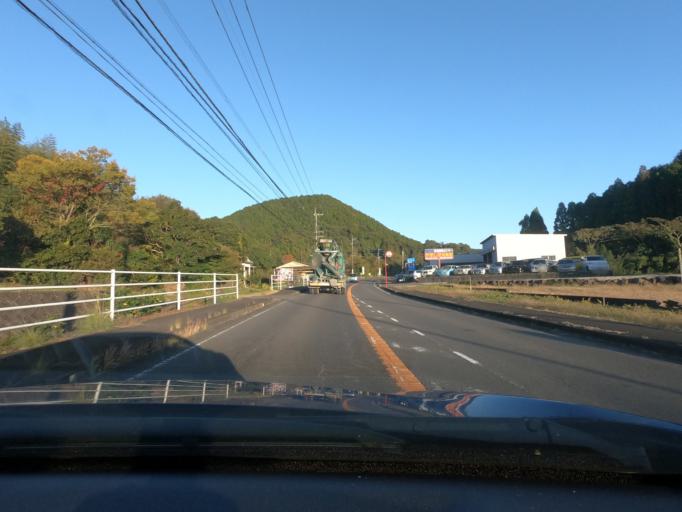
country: JP
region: Kagoshima
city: Satsumasendai
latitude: 31.8055
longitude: 130.3517
